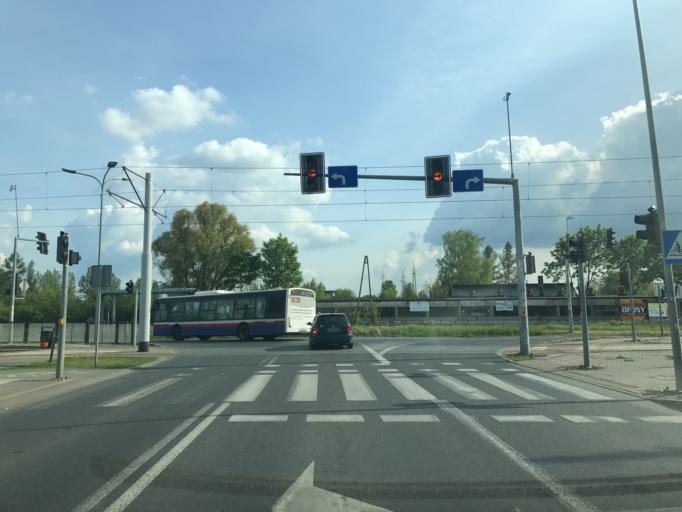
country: PL
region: Kujawsko-Pomorskie
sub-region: Powiat bydgoski
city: Osielsko
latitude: 53.1185
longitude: 18.0873
